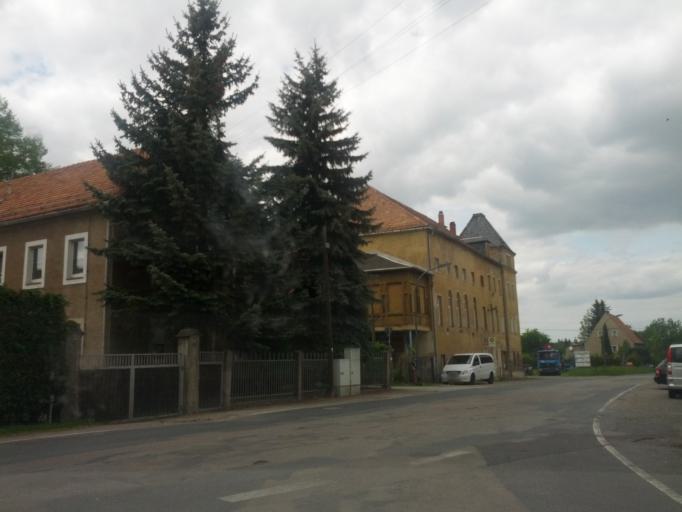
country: DE
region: Saxony
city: Kreischa
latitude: 50.9345
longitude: 13.7729
